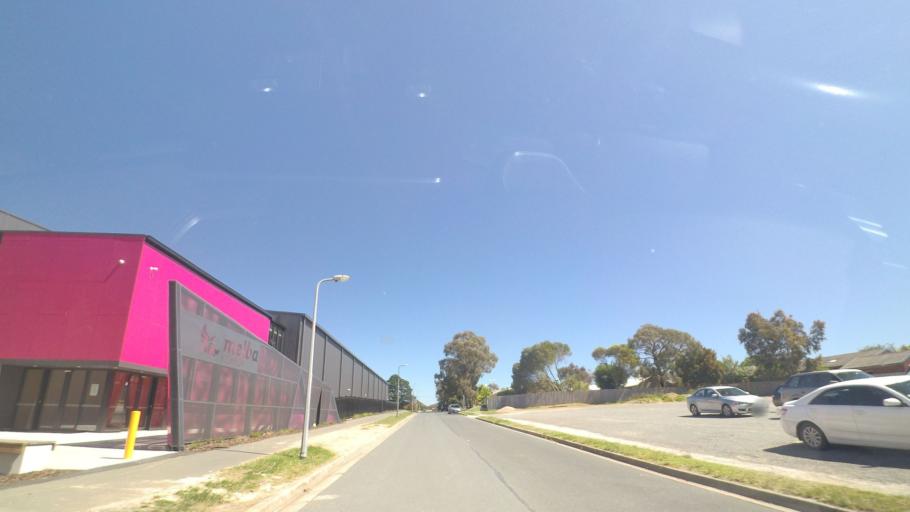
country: AU
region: Victoria
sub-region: Maroondah
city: Croydon South
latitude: -37.7950
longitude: 145.2625
